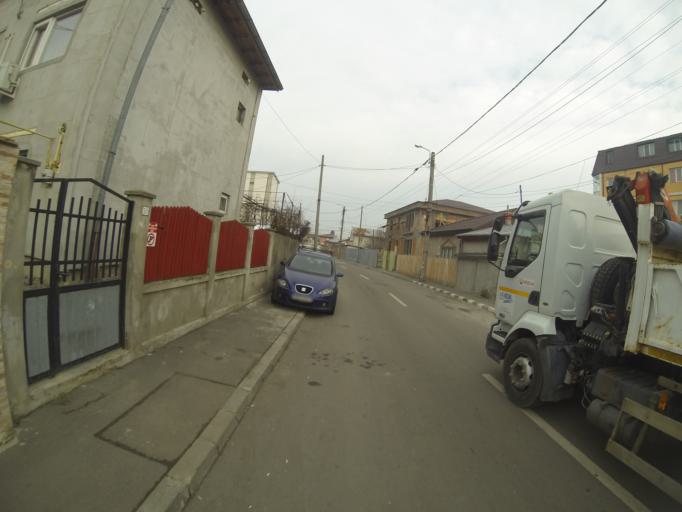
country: RO
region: Bucuresti
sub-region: Municipiul Bucuresti
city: Bucuresti
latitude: 44.3983
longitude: 26.0727
